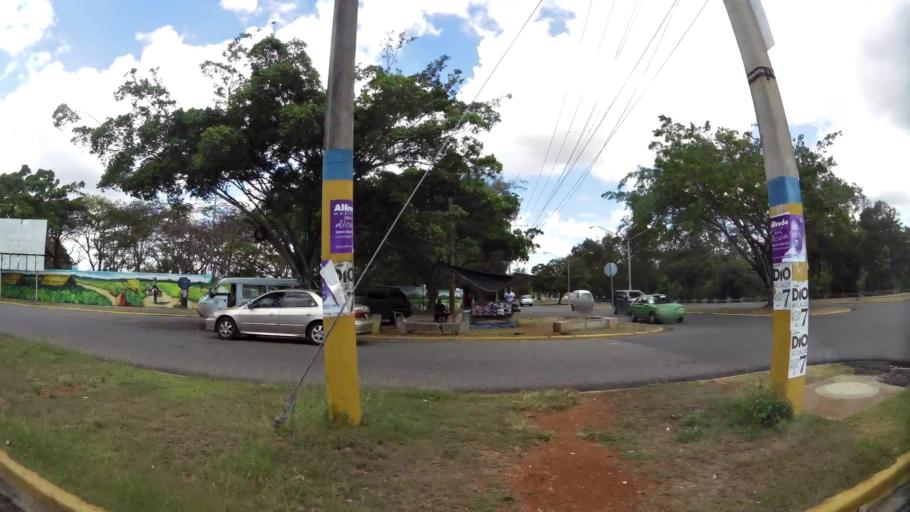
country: DO
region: Santo Domingo
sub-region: Santo Domingo
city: Santo Domingo Este
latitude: 18.4784
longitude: -69.8442
